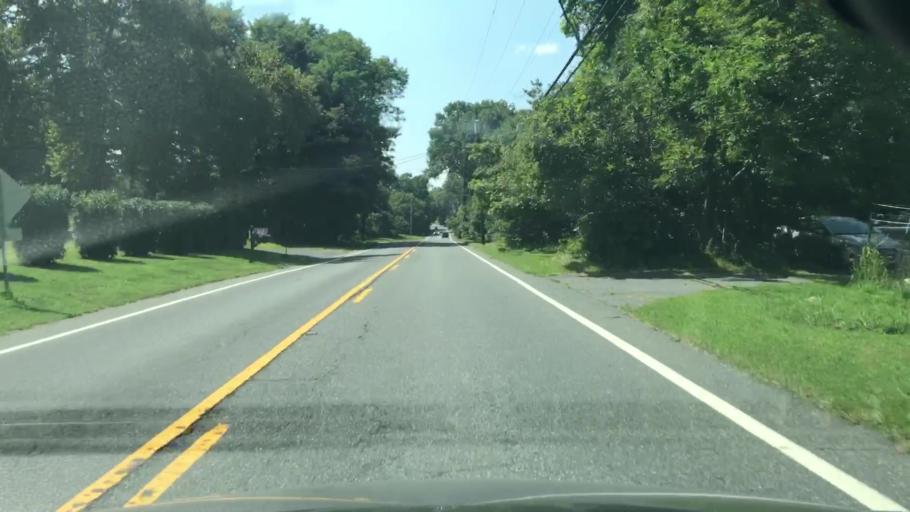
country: US
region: New Jersey
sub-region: Hunterdon County
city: Milford
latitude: 40.6323
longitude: -75.0270
